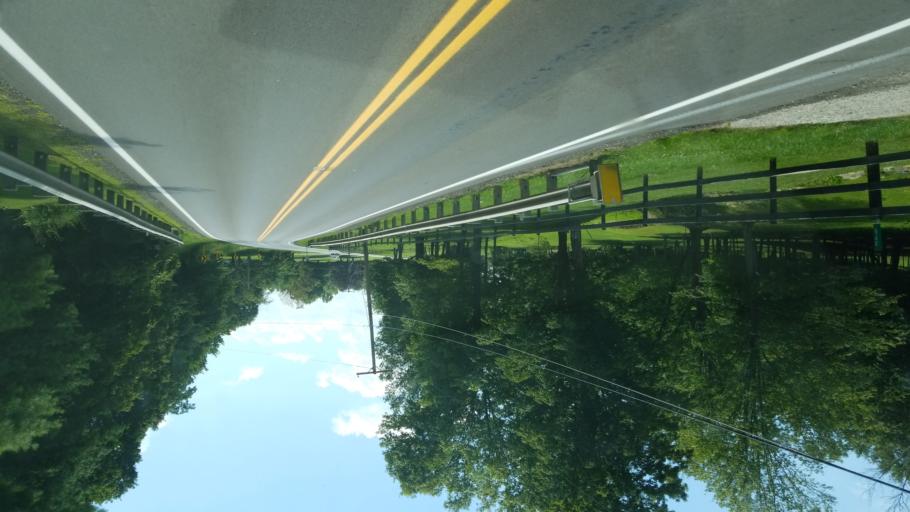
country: US
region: Ohio
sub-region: Richland County
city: Ontario
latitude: 40.7494
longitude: -82.6618
